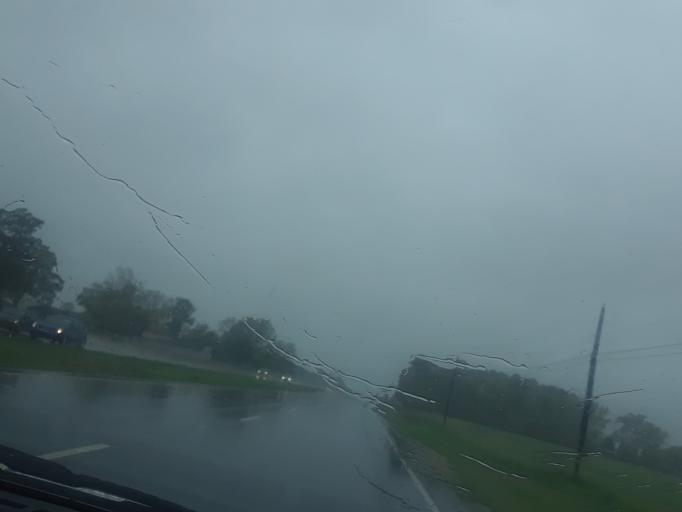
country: US
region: North Carolina
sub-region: Harnett County
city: Erwin
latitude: 35.3595
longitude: -78.6989
